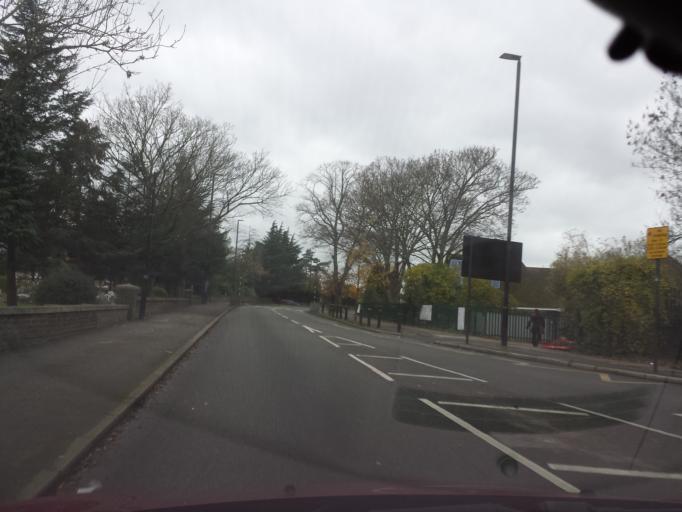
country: GB
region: England
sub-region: Greater London
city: Feltham
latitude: 51.4380
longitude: -0.4215
